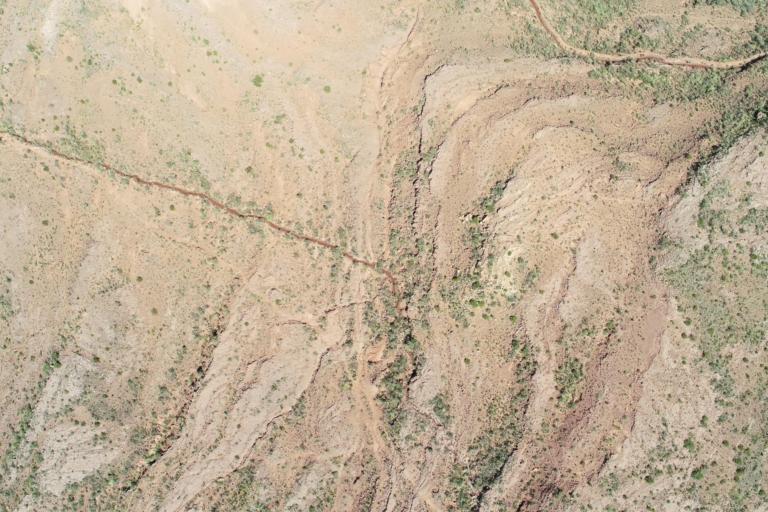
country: BO
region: La Paz
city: Tiahuanaco
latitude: -16.5981
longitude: -68.7569
